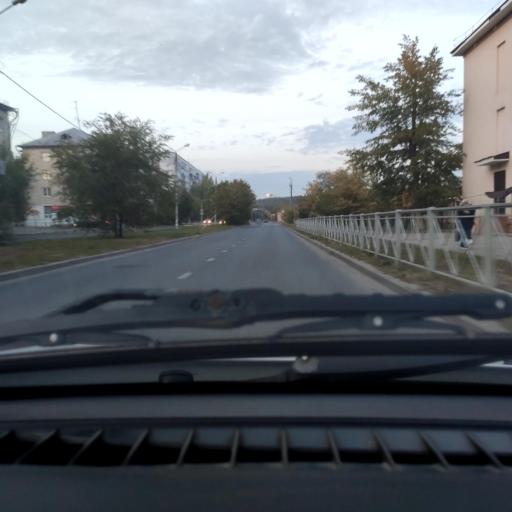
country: RU
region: Samara
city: Zhigulevsk
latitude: 53.4666
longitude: 49.5362
